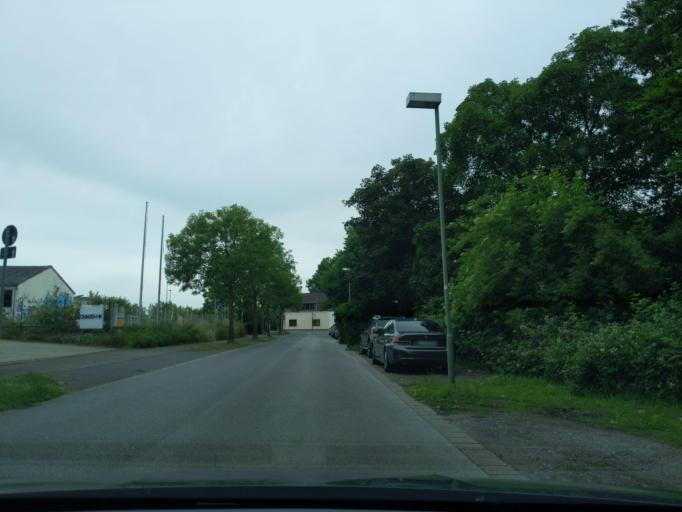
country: DE
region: North Rhine-Westphalia
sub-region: Regierungsbezirk Dusseldorf
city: Kaarst
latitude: 51.2670
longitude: 6.6316
